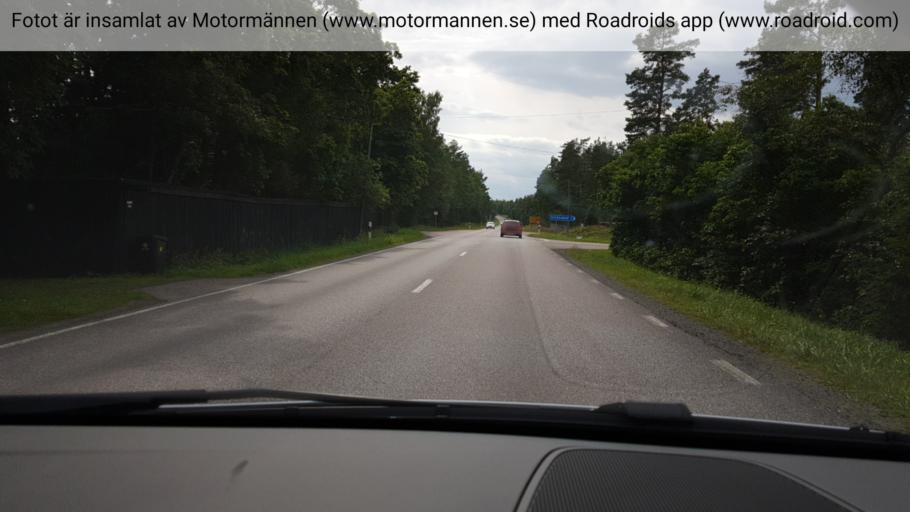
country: SE
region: Uppsala
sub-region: Osthammars Kommun
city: OEsthammar
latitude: 60.3200
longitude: 18.3087
